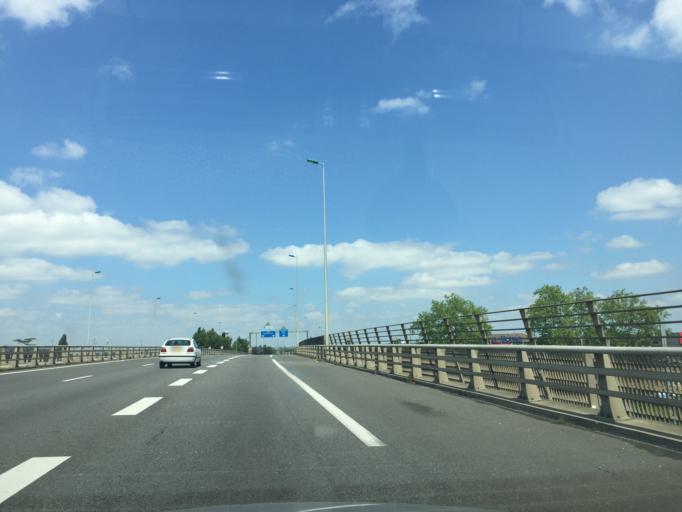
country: FR
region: Midi-Pyrenees
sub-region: Departement de la Haute-Garonne
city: Aucamville
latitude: 43.6515
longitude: 1.4234
